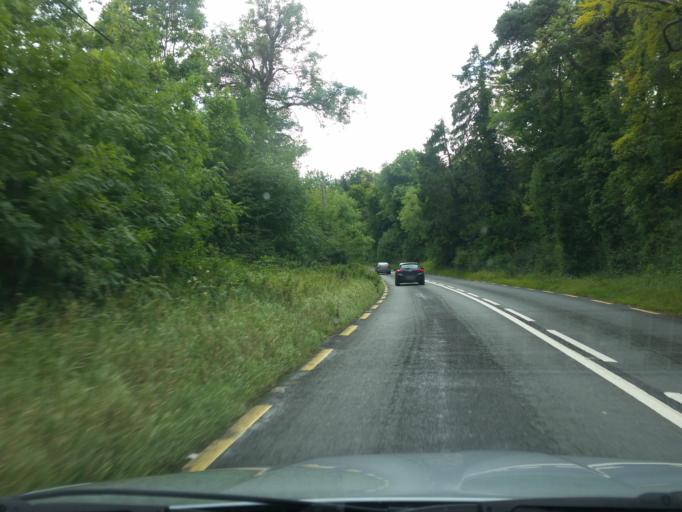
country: IE
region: Ulster
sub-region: An Cabhan
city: Belturbet
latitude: 54.0968
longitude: -7.3692
